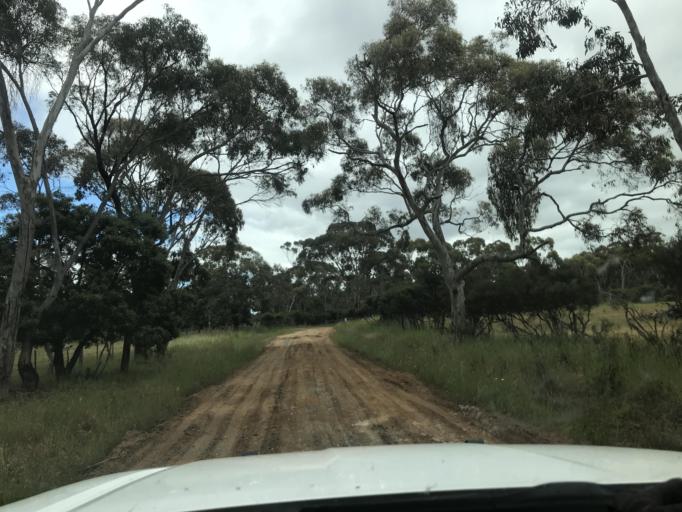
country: AU
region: South Australia
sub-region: Wattle Range
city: Penola
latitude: -37.1215
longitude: 141.2156
